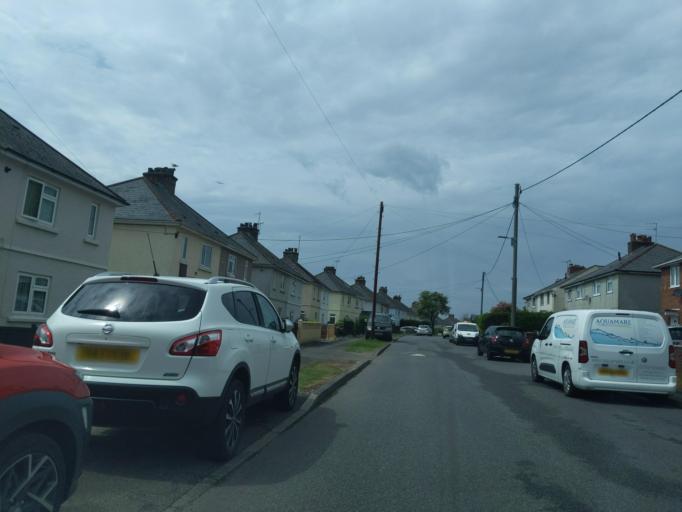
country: GB
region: England
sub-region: Devon
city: Plympton
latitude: 50.3920
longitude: -4.0610
